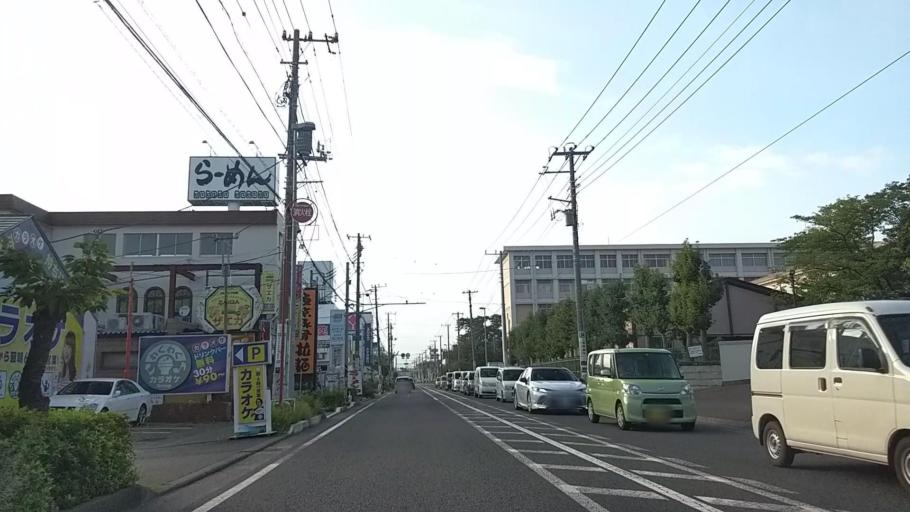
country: JP
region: Kanagawa
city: Hiratsuka
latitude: 35.3304
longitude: 139.3274
